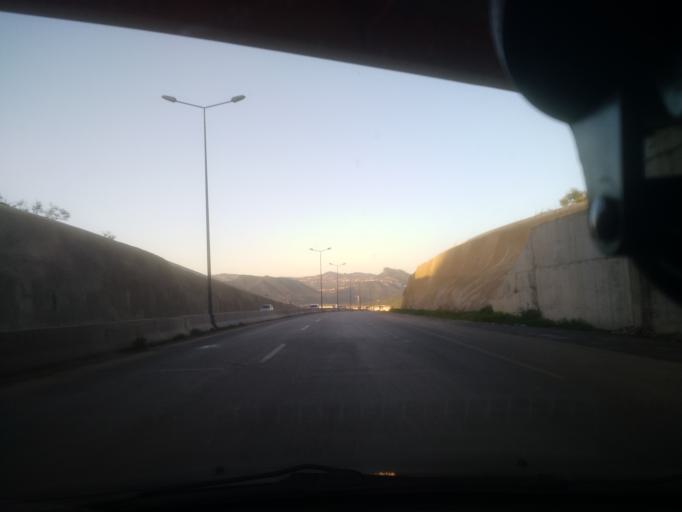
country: DZ
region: Boumerdes
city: Draa Ben Khedda
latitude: 36.7344
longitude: 3.9991
